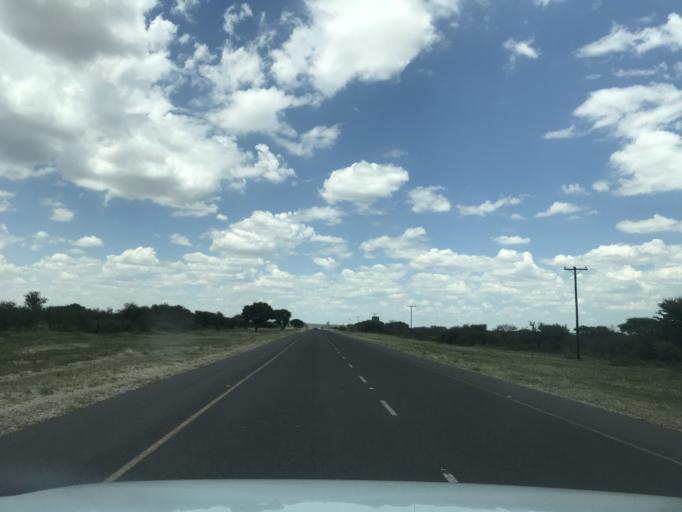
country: BW
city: Mabuli
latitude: -25.7235
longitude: 25.1146
